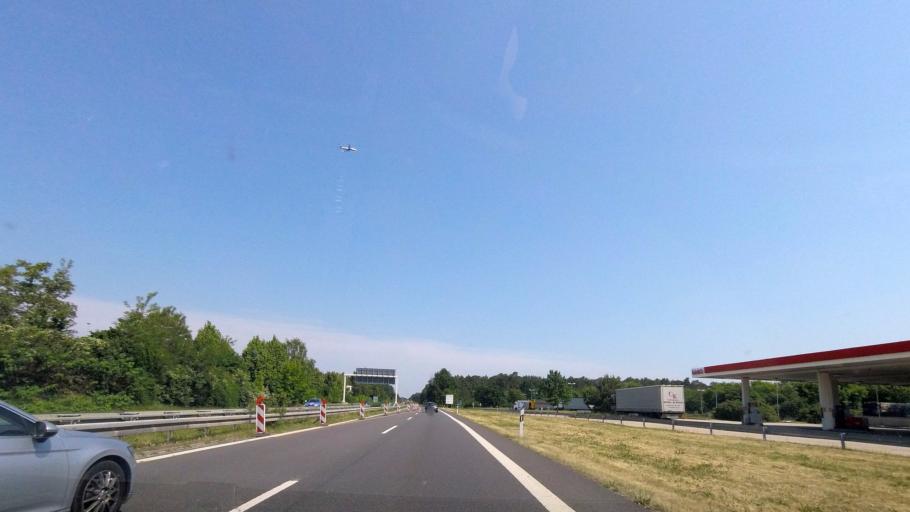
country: DE
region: Berlin
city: Bohnsdorf
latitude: 52.3772
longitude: 13.5620
